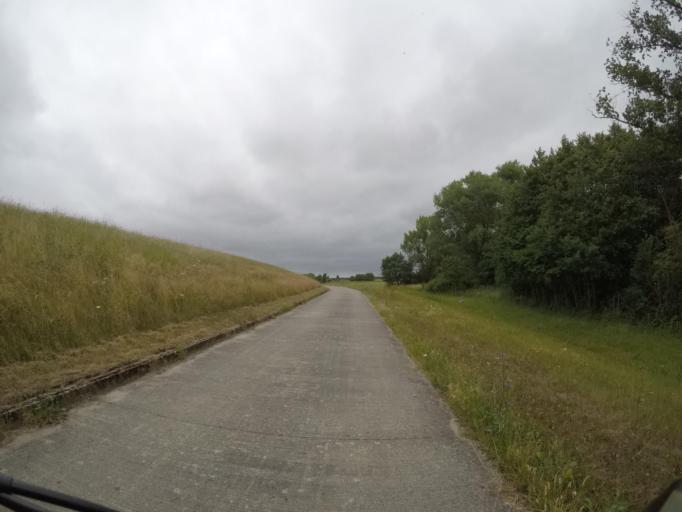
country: DE
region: Lower Saxony
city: Hitzacker
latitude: 53.1552
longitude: 11.0720
